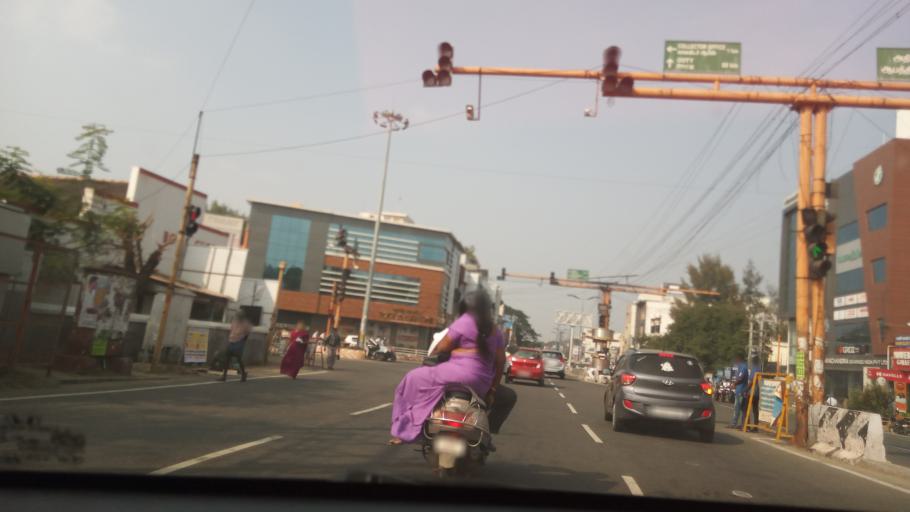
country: IN
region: Tamil Nadu
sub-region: Coimbatore
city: Coimbatore
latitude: 11.0027
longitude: 76.9686
